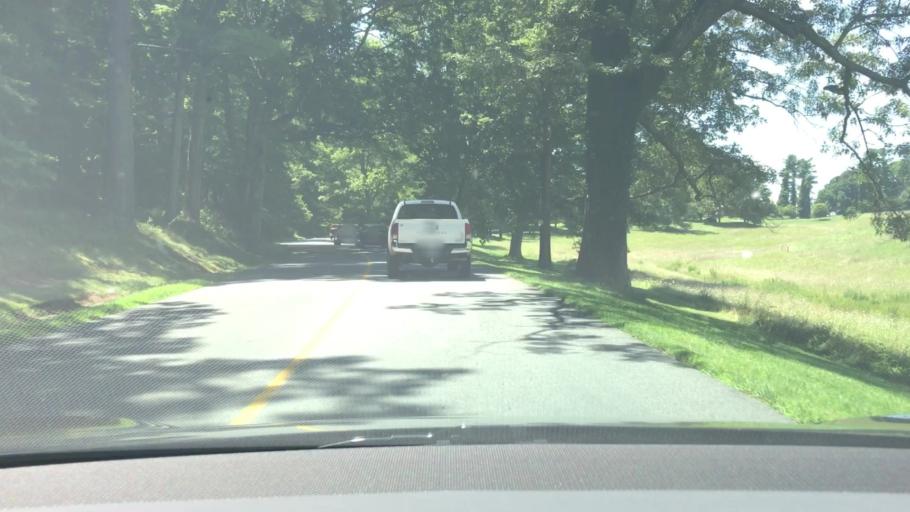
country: US
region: North Carolina
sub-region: Buncombe County
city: Asheville
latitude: 35.5581
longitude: -82.5726
